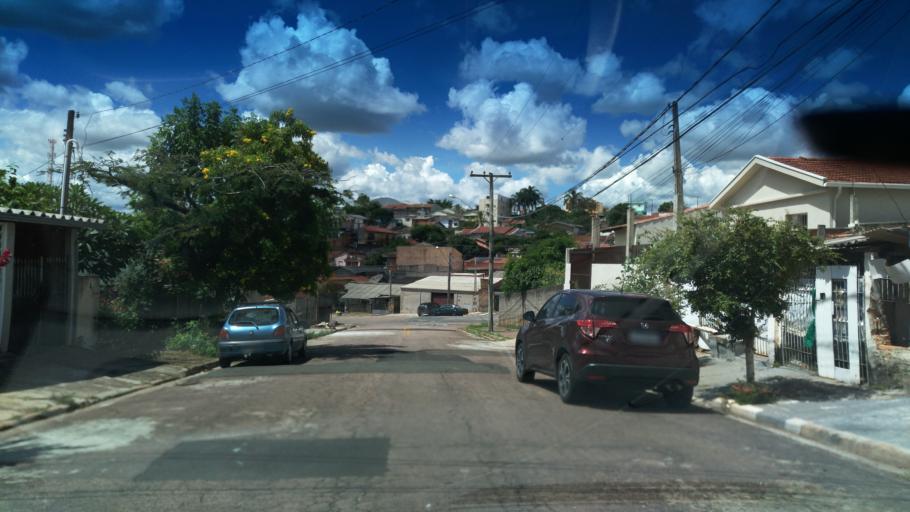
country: BR
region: Sao Paulo
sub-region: Valinhos
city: Valinhos
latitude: -22.9552
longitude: -47.0064
